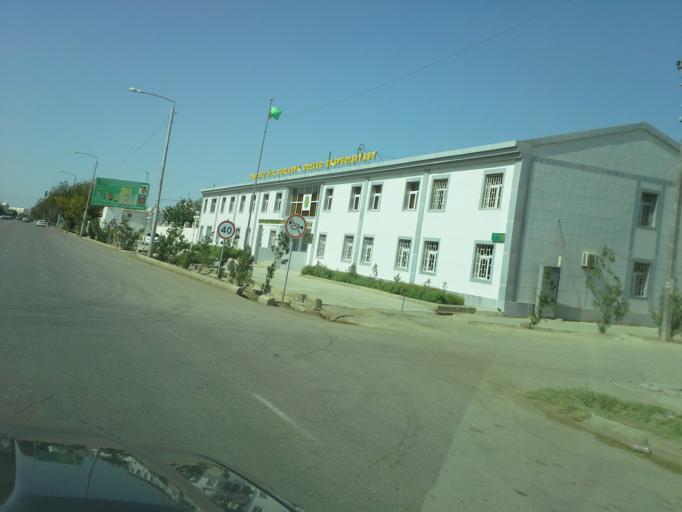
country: TM
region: Dasoguz
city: Dasoguz
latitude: 41.8173
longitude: 59.9846
